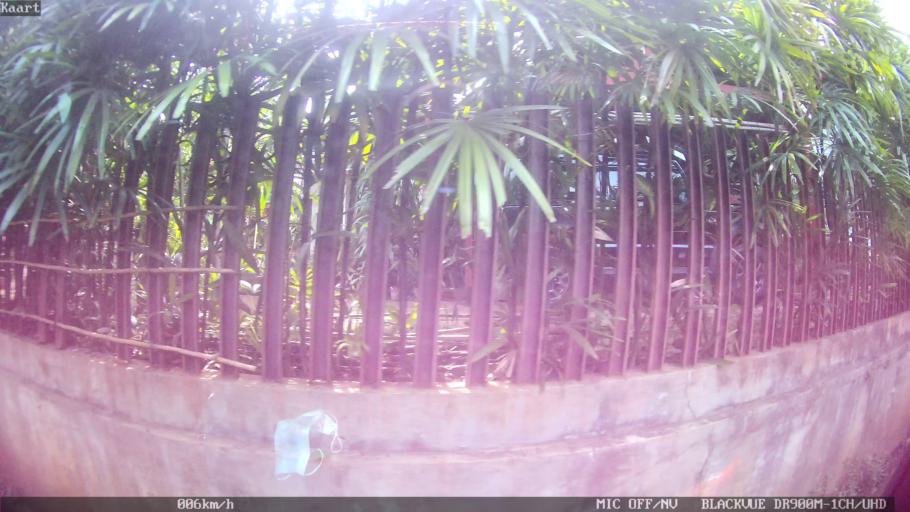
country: ID
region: Lampung
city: Bandarlampung
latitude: -5.4333
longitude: 105.2685
